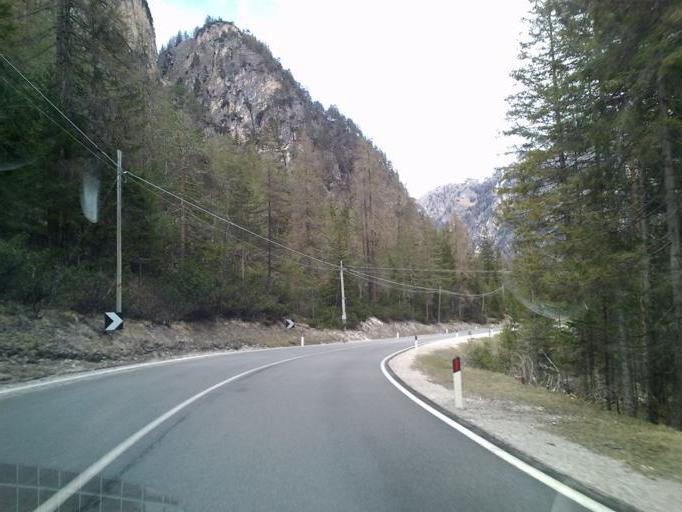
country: IT
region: Trentino-Alto Adige
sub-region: Bolzano
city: Dobbiaco
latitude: 46.6379
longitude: 12.2304
